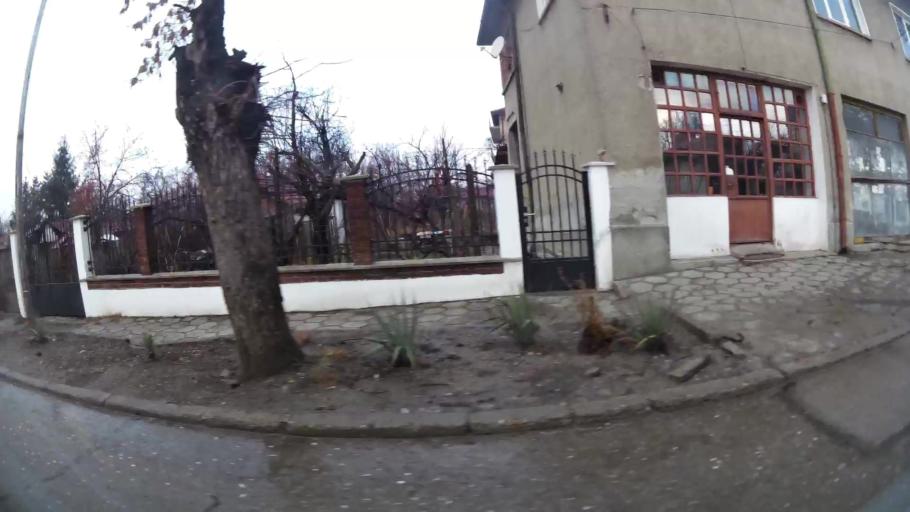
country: BG
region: Sofia-Capital
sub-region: Stolichna Obshtina
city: Sofia
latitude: 42.7370
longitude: 23.3433
